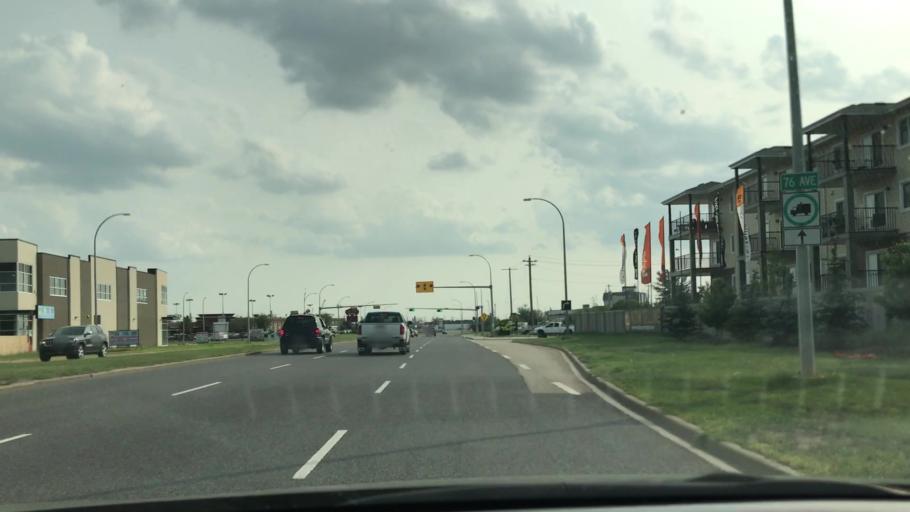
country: CA
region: Alberta
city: Edmonton
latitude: 53.5138
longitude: -113.4356
